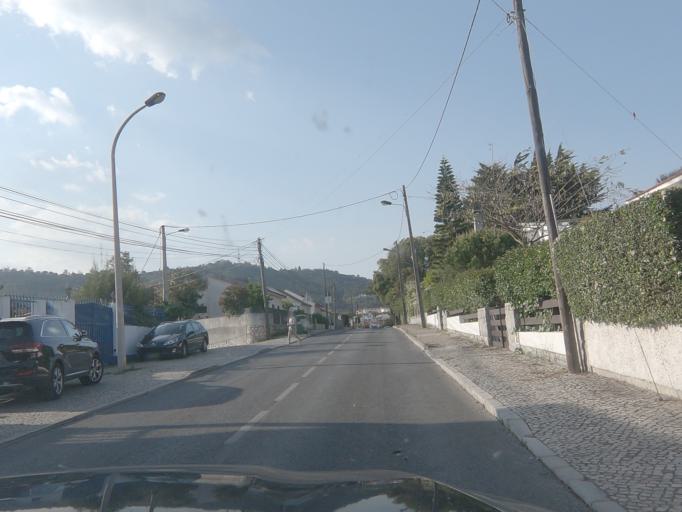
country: PT
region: Setubal
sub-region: Setubal
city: Setubal
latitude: 38.5430
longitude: -8.8983
